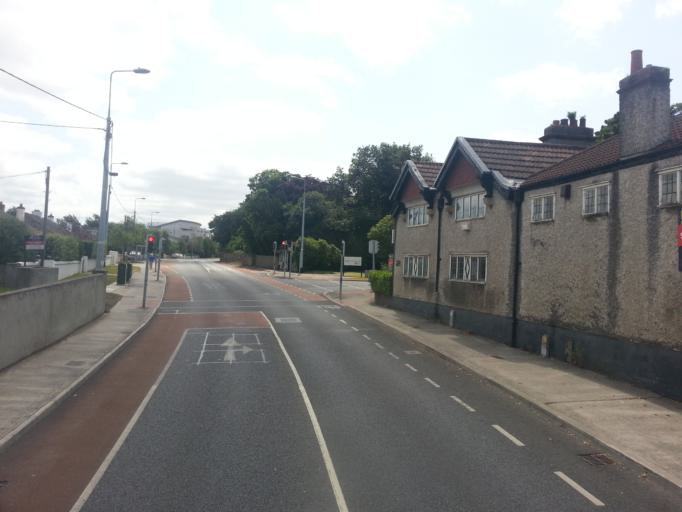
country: IE
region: Leinster
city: Balally
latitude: 53.2779
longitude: -6.2311
